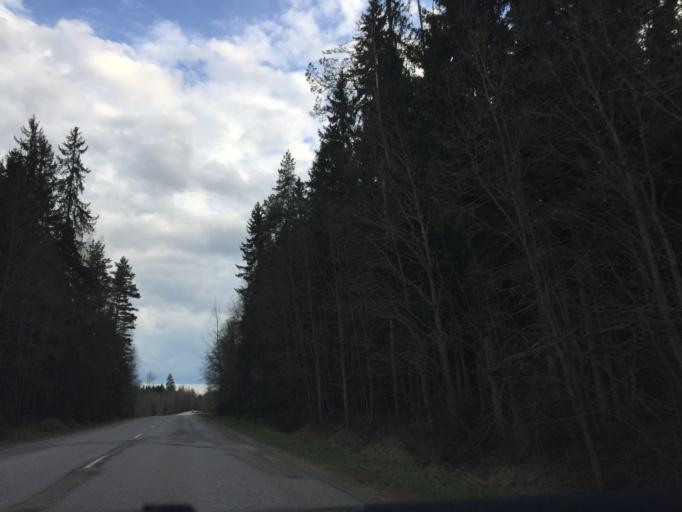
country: LV
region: Aluksnes Rajons
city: Aluksne
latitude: 57.3138
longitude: 27.0713
